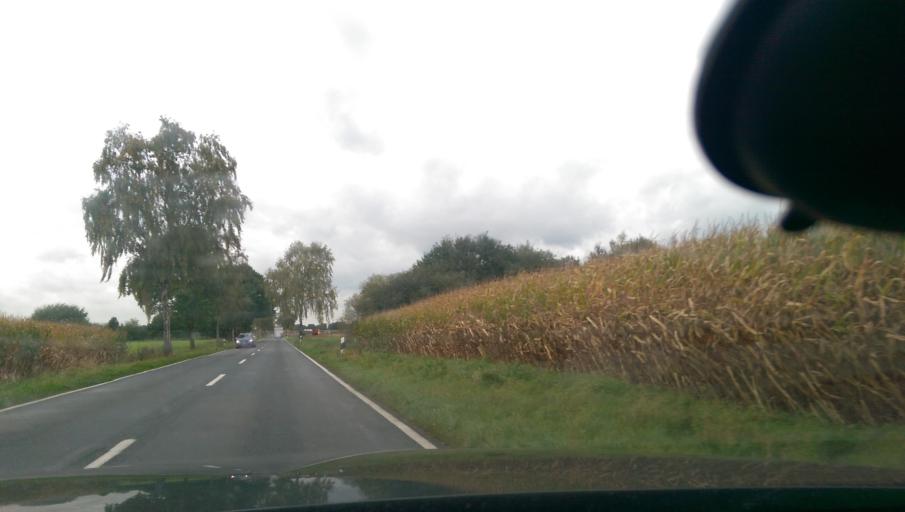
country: DE
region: Lower Saxony
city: Isernhagen Farster Bauerschaft
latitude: 52.4796
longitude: 9.8983
